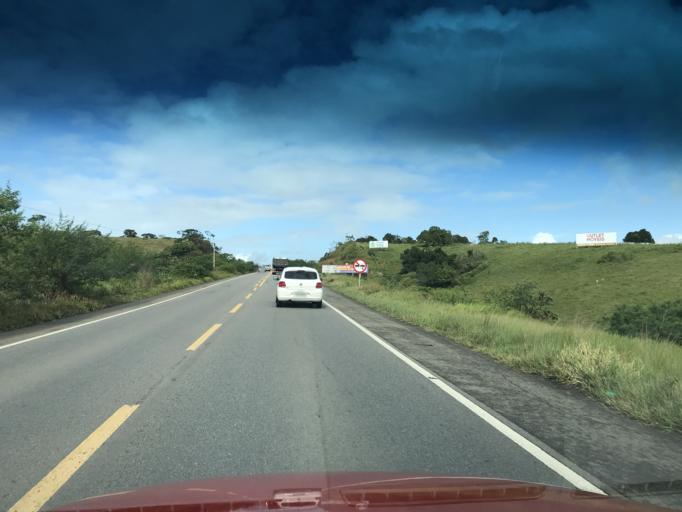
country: BR
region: Bahia
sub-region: Conceicao Do Almeida
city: Muritiba
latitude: -12.9096
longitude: -39.2403
